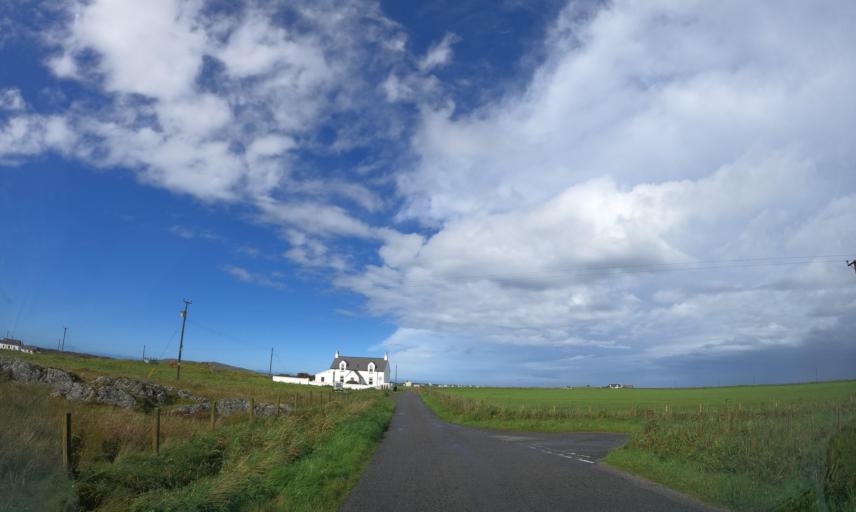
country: GB
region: Scotland
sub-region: Eilean Siar
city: Barra
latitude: 56.5208
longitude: -6.8953
